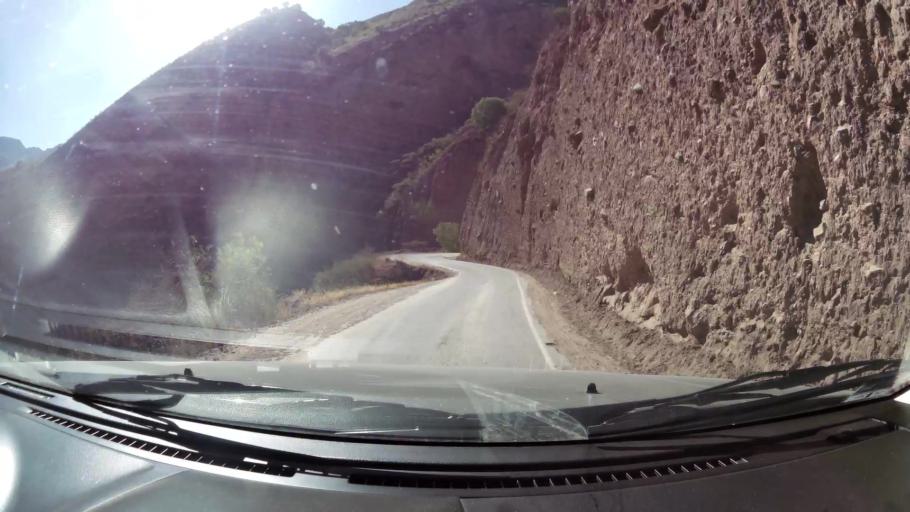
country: PE
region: Huancavelica
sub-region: Provincia de Acobamba
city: Pomacocha
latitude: -12.7860
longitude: -74.4895
